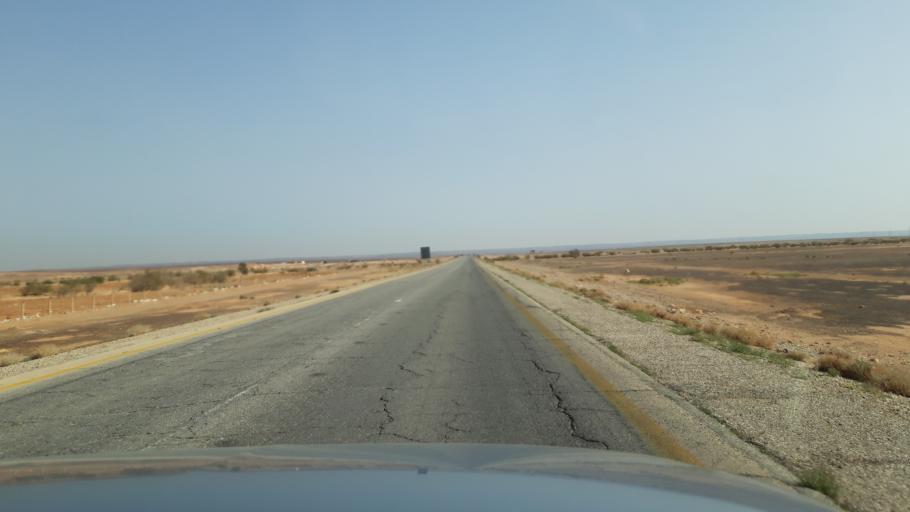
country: JO
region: Amman
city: Al Azraq ash Shamali
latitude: 31.7956
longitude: 36.5858
